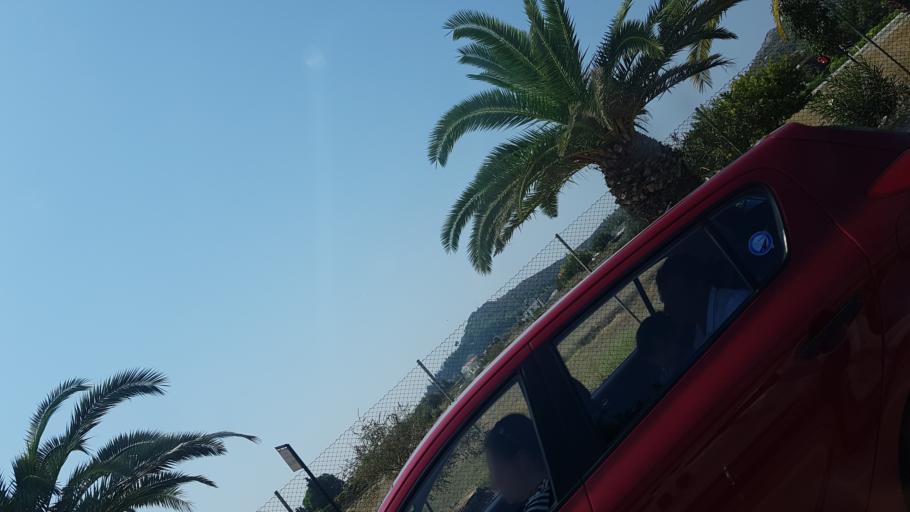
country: TR
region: Izmir
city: Urla
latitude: 38.3627
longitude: 26.7704
